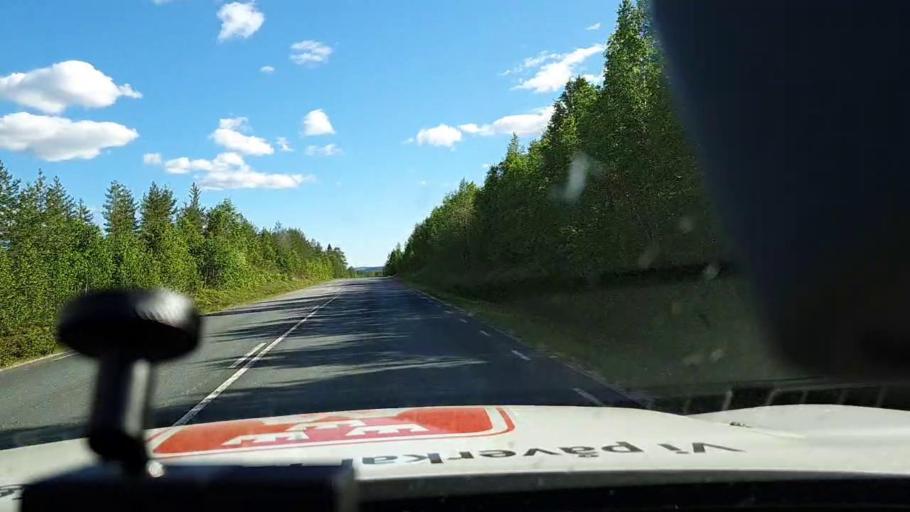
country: SE
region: Norrbotten
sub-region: Overtornea Kommun
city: OEvertornea
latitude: 66.3507
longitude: 23.6479
